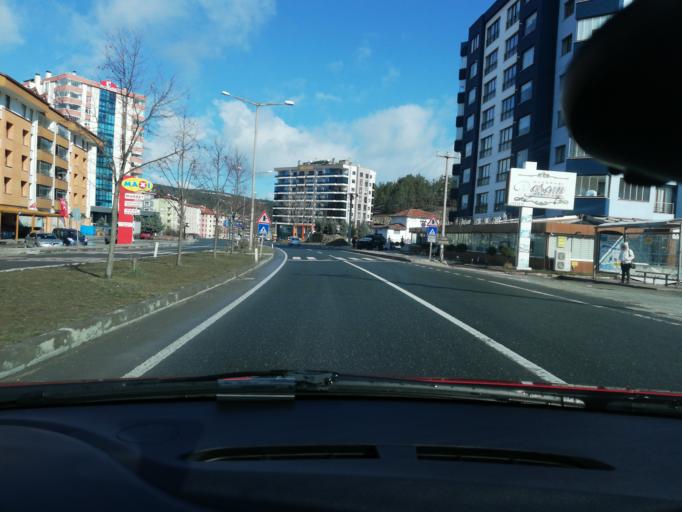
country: TR
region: Kastamonu
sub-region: Cide
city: Kastamonu
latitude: 41.3593
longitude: 33.7681
